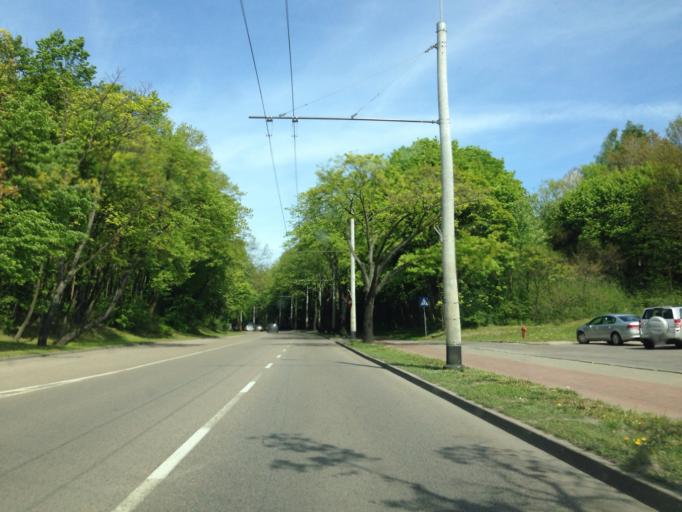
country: PL
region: Pomeranian Voivodeship
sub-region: Sopot
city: Sopot
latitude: 54.4685
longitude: 18.5558
